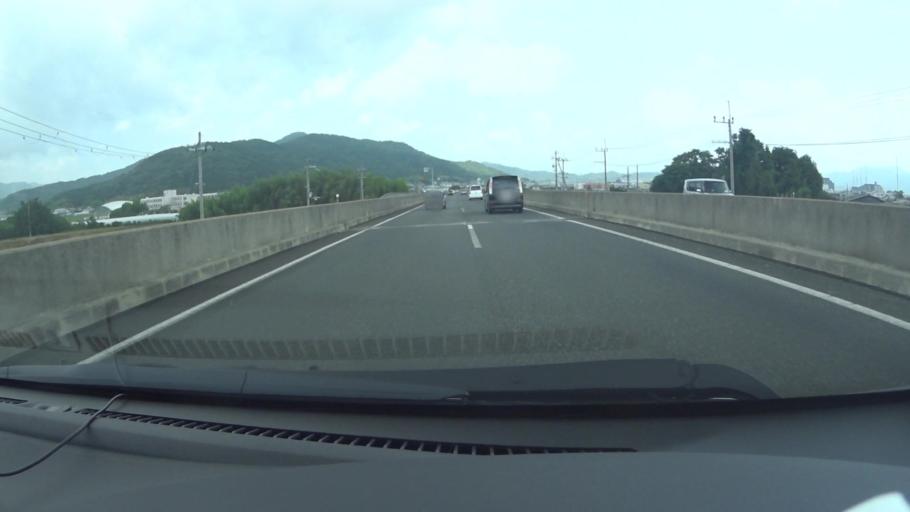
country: JP
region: Kyoto
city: Kameoka
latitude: 35.0204
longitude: 135.5519
